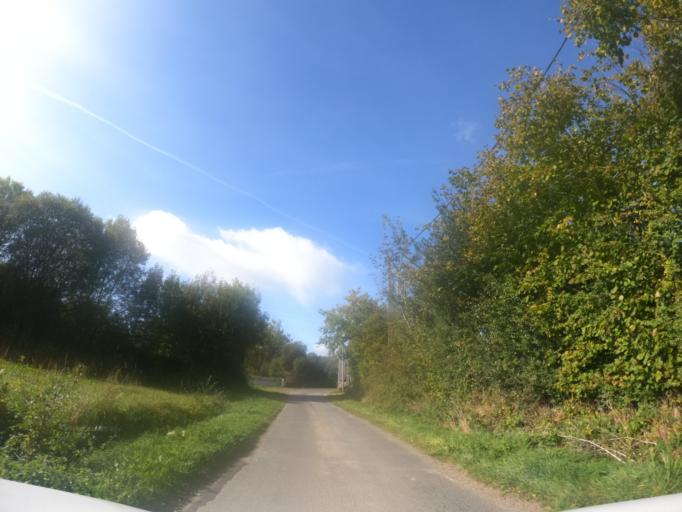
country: FR
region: Poitou-Charentes
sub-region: Departement des Deux-Sevres
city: Courlay
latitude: 46.7920
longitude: -0.5851
